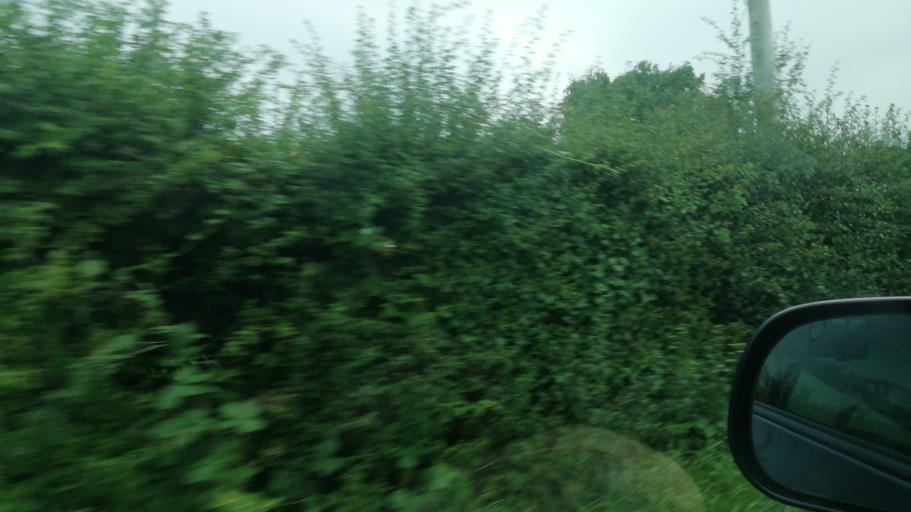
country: IE
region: Munster
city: Fethard
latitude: 52.5184
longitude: -7.6837
